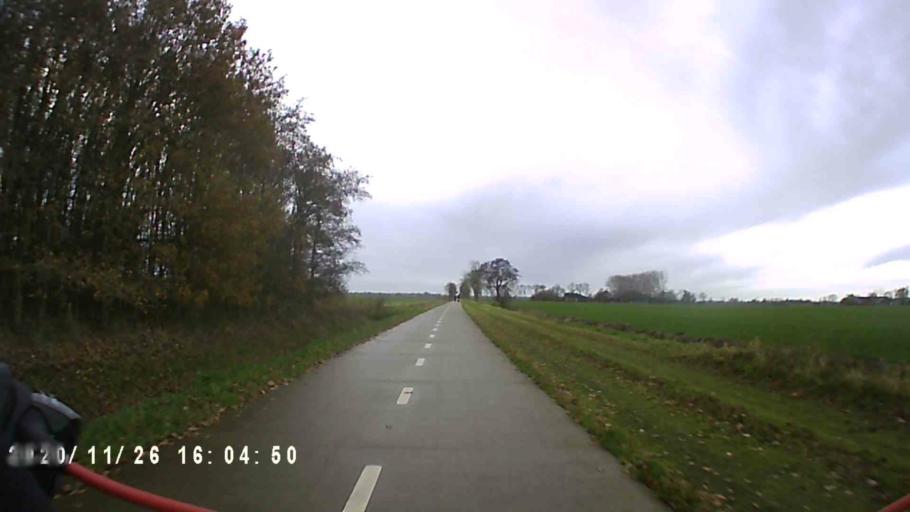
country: NL
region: Groningen
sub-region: Gemeente Bedum
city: Bedum
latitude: 53.2684
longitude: 6.6771
